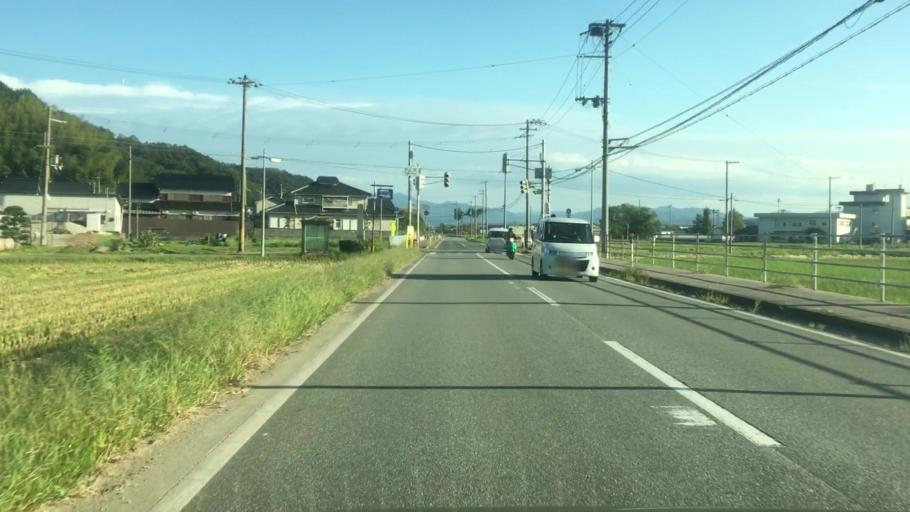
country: JP
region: Hyogo
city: Toyooka
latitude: 35.5656
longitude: 134.8198
